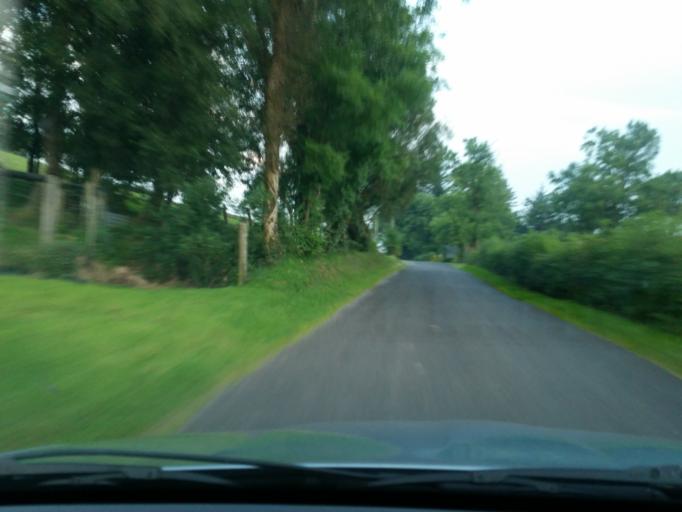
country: GB
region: Northern Ireland
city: Fivemiletown
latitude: 54.3017
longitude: -7.2916
